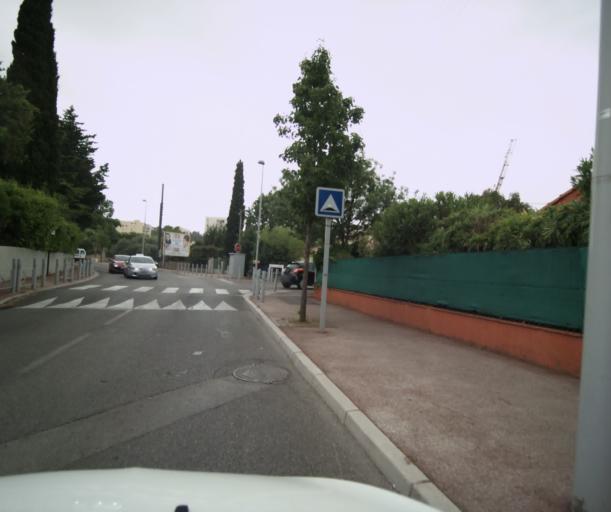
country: FR
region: Provence-Alpes-Cote d'Azur
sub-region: Departement du Var
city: La Valette-du-Var
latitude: 43.1316
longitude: 5.9883
